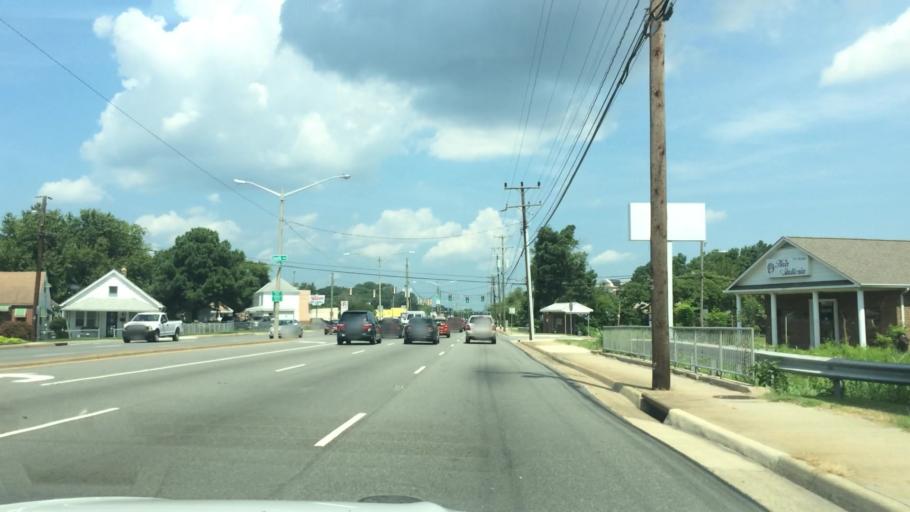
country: US
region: Virginia
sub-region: City of Newport News
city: Newport News
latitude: 37.0263
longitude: -76.4487
